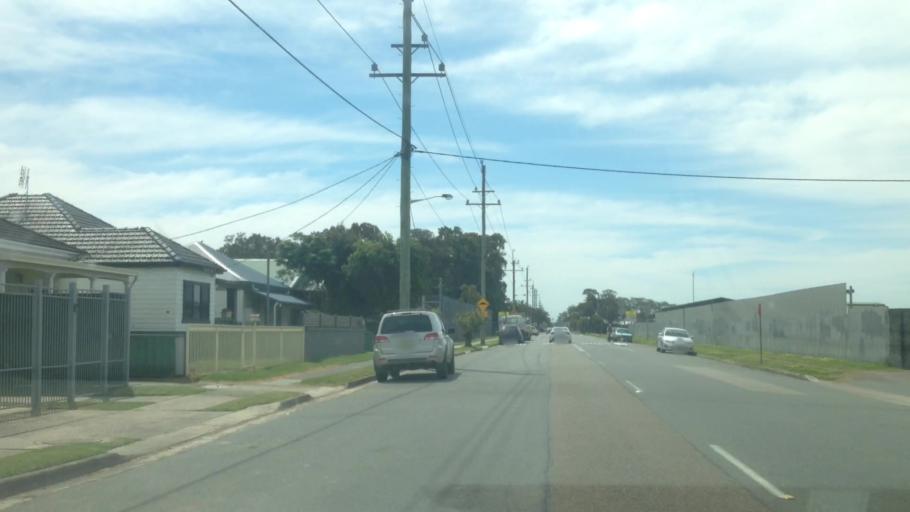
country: AU
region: New South Wales
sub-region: Newcastle
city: Broadmeadow
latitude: -32.9315
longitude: 151.7360
